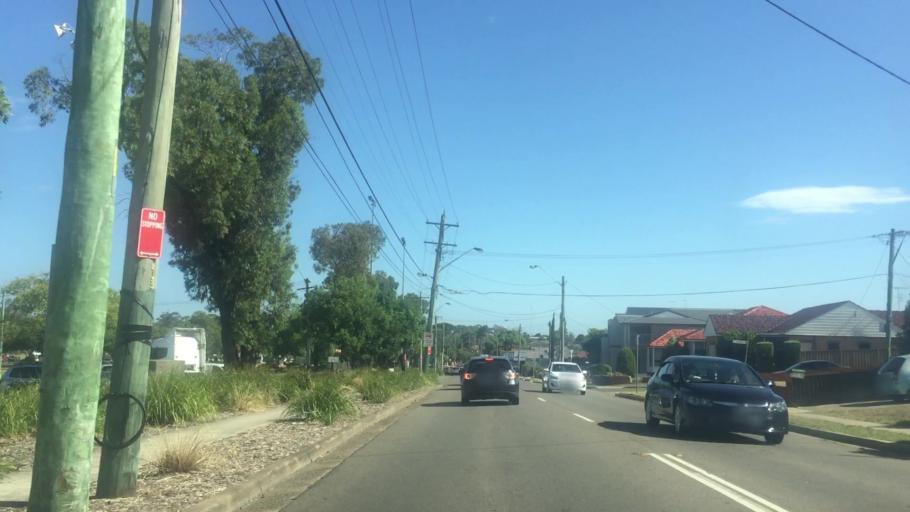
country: AU
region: New South Wales
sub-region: Holroyd
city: Merrylands
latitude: -33.8319
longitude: 150.9776
